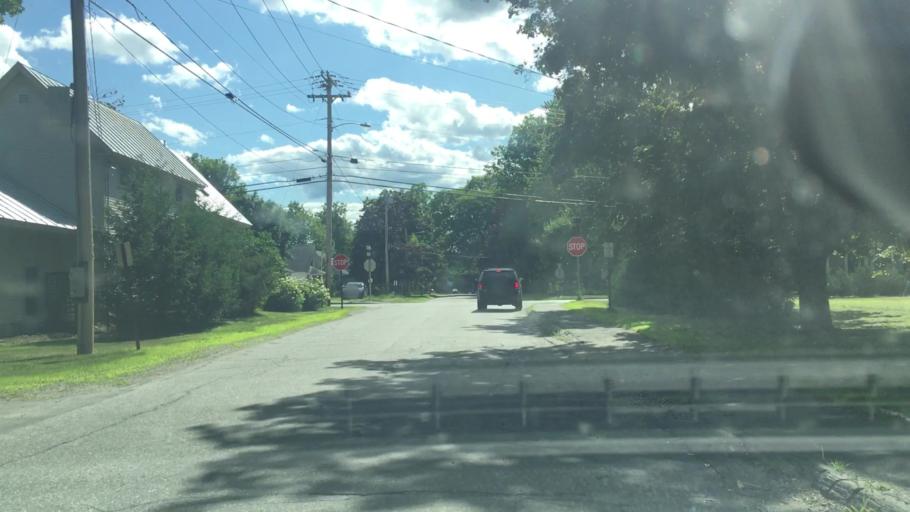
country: US
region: Maine
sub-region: Franklin County
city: Farmington
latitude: 44.6633
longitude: -70.1412
